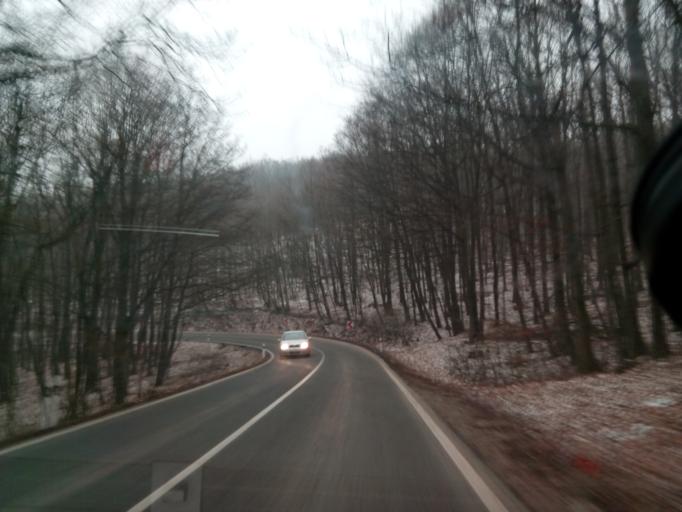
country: SK
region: Kosicky
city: Kosice
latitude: 48.7126
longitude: 21.1938
